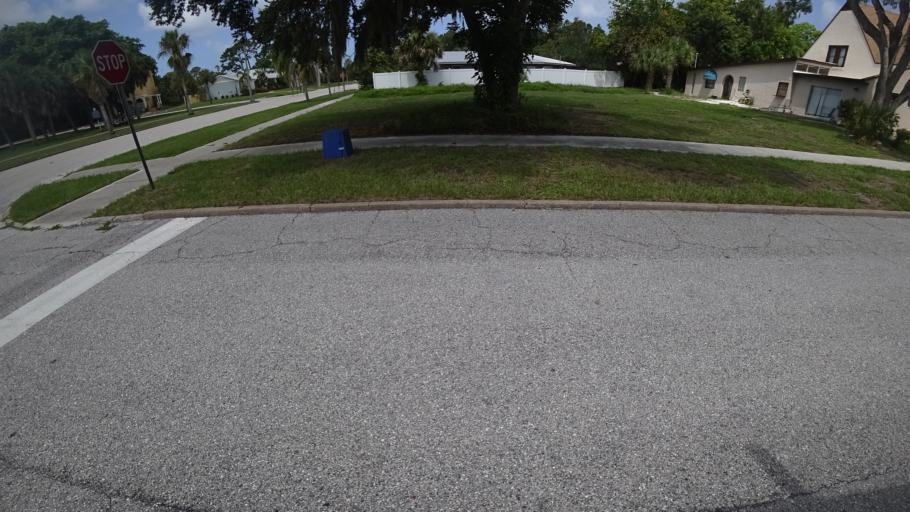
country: US
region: Florida
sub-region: Manatee County
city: Whitfield
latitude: 27.4087
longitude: -82.5727
